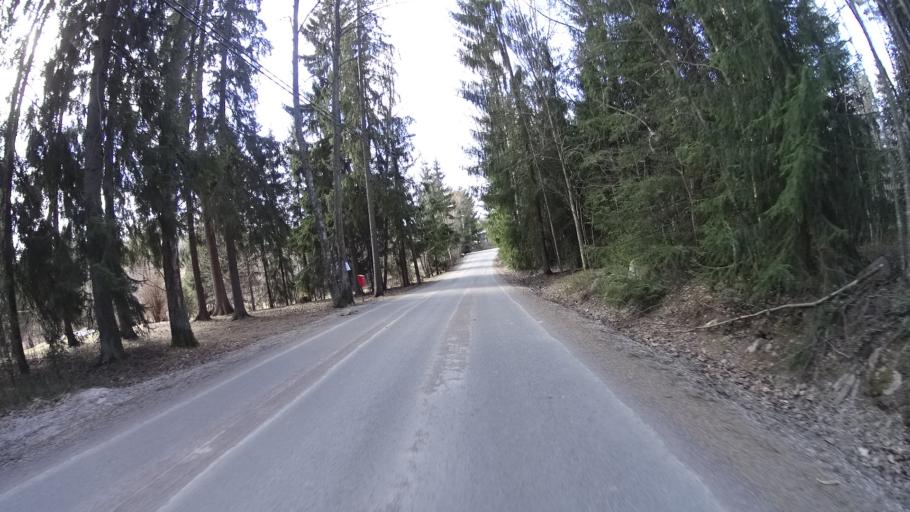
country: FI
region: Uusimaa
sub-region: Helsinki
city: Kauniainen
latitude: 60.2759
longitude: 24.7201
